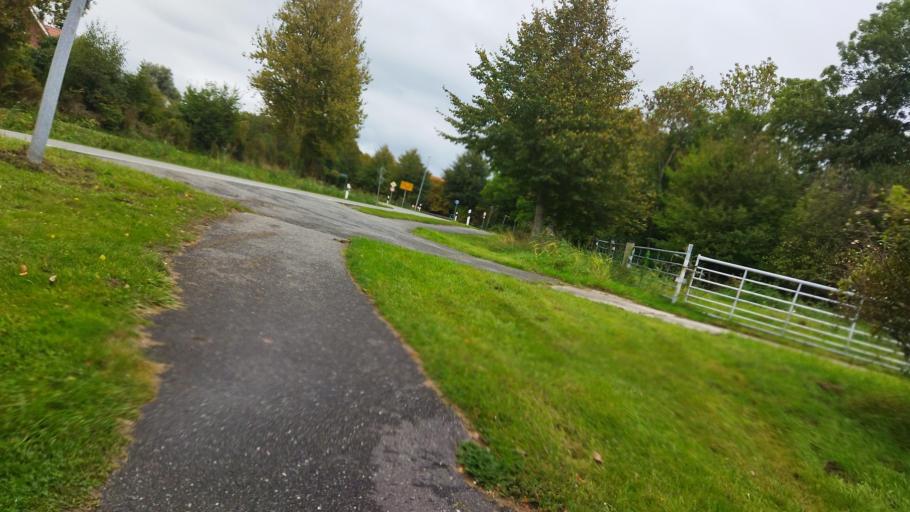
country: DE
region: Lower Saxony
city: Wirdum
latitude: 53.4725
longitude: 7.1384
